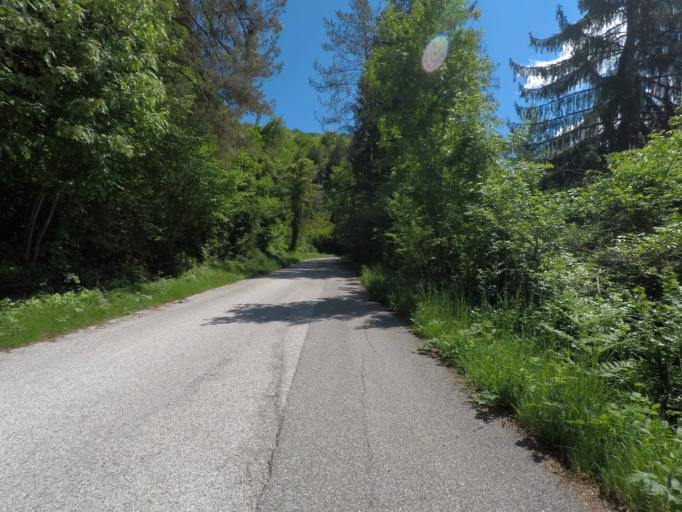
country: IT
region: Friuli Venezia Giulia
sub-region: Provincia di Udine
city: Raveo
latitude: 46.4435
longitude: 12.8807
